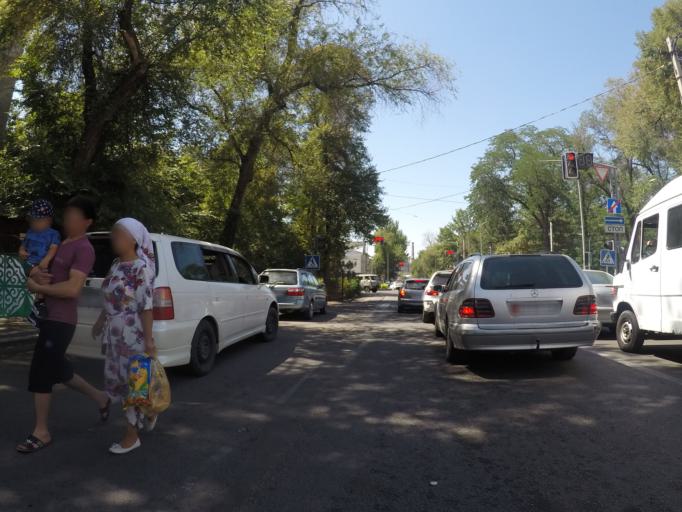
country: KG
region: Chuy
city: Bishkek
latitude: 42.8683
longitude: 74.5757
